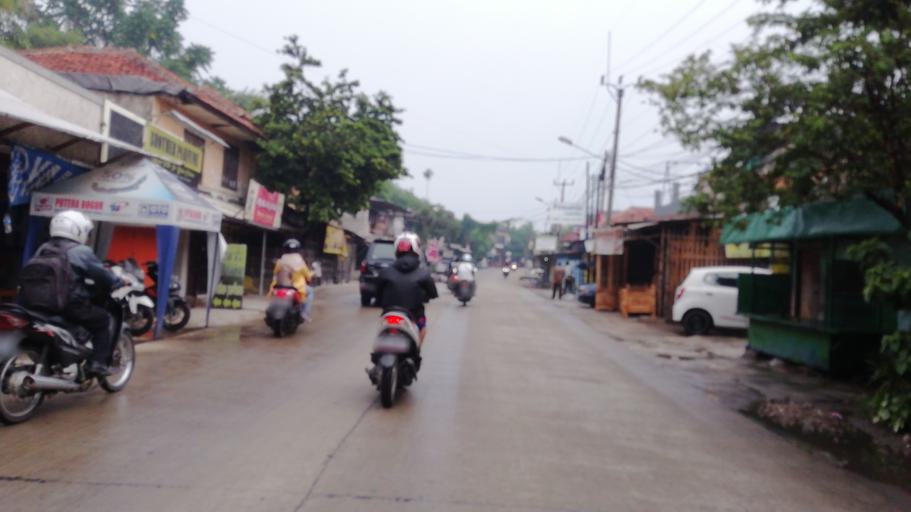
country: ID
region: West Java
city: Bogor
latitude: -6.5574
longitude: 106.8128
